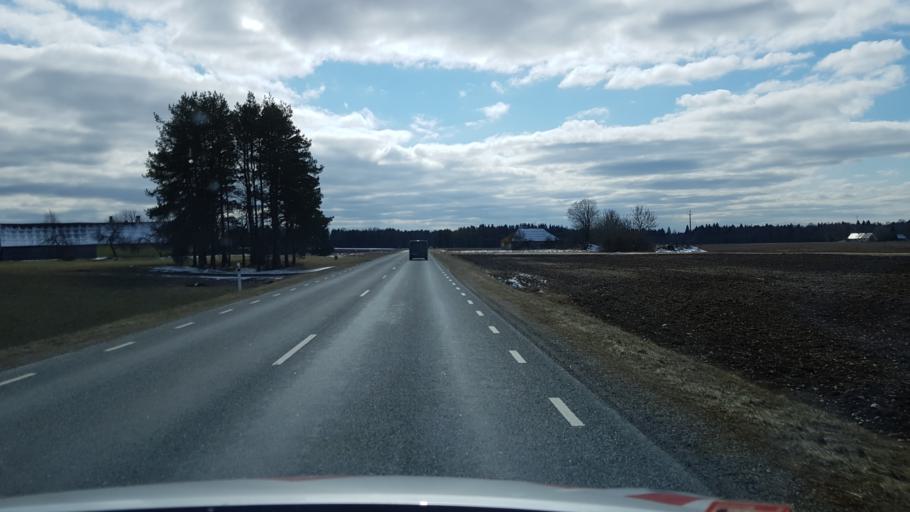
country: EE
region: Laeaene-Virumaa
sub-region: Tapa vald
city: Tapa
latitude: 59.2945
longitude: 25.9983
